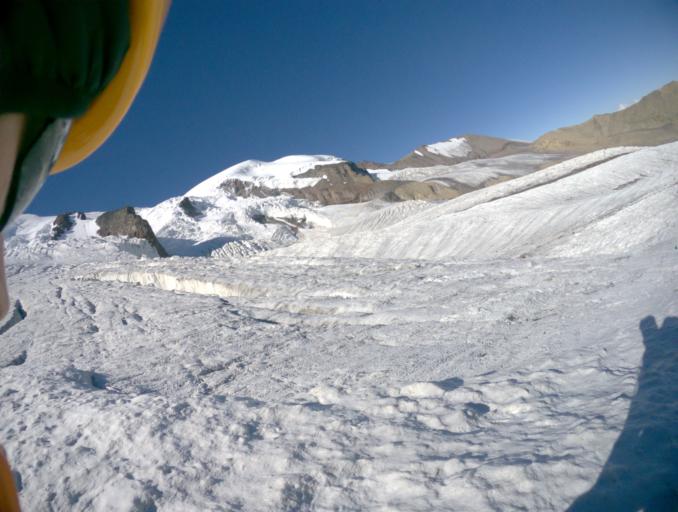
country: RU
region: Kabardino-Balkariya
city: Terskol
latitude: 43.3874
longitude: 42.4352
